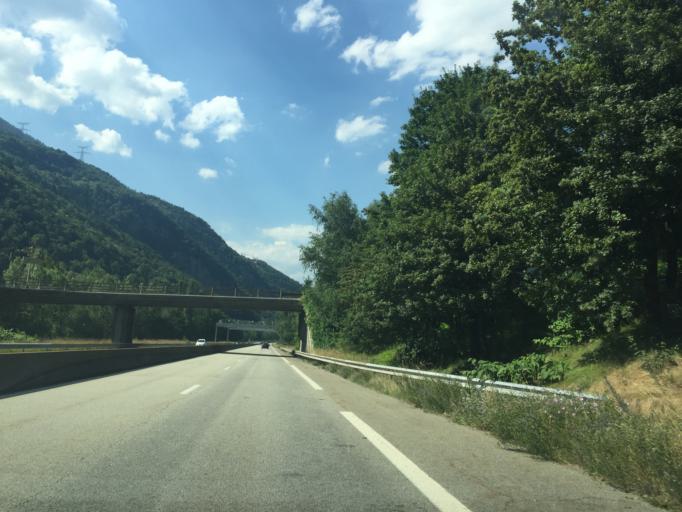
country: FR
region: Rhone-Alpes
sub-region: Departement de la Savoie
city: Aigueblanche
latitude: 45.5542
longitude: 6.4685
